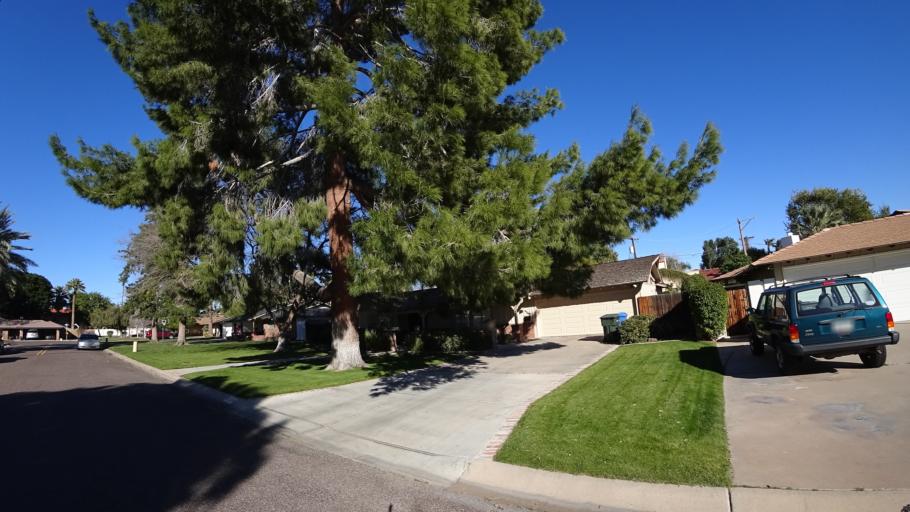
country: US
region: Arizona
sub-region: Maricopa County
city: Phoenix
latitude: 33.5361
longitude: -112.0758
